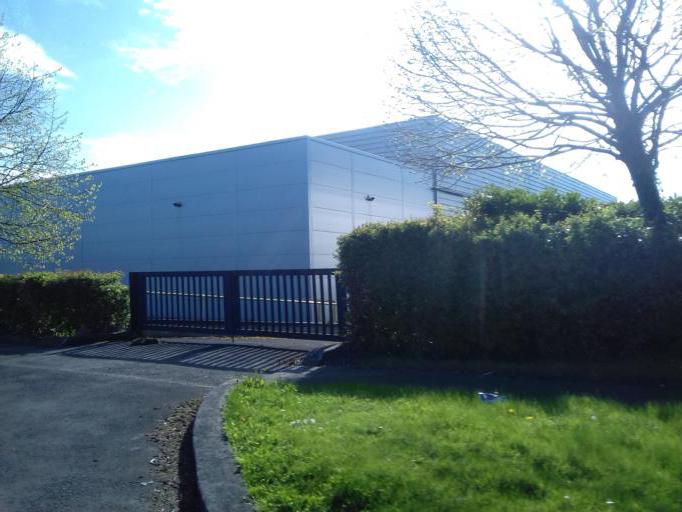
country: IE
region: Leinster
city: Castleknock
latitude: 53.3996
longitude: -6.3397
